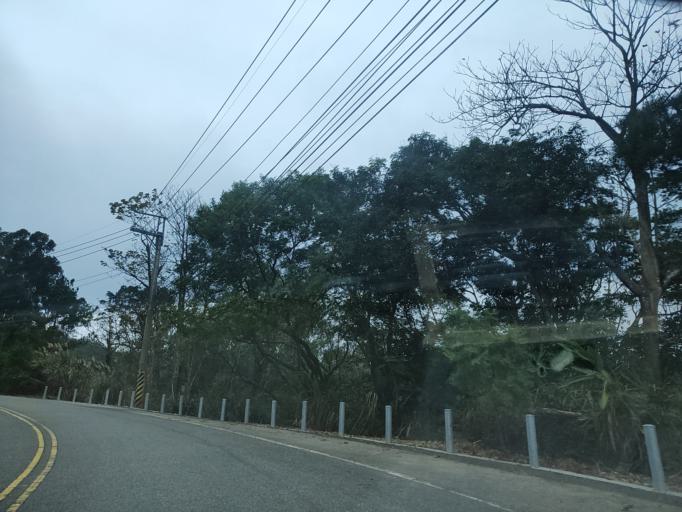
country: TW
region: Taiwan
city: Fengyuan
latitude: 24.3743
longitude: 120.7751
